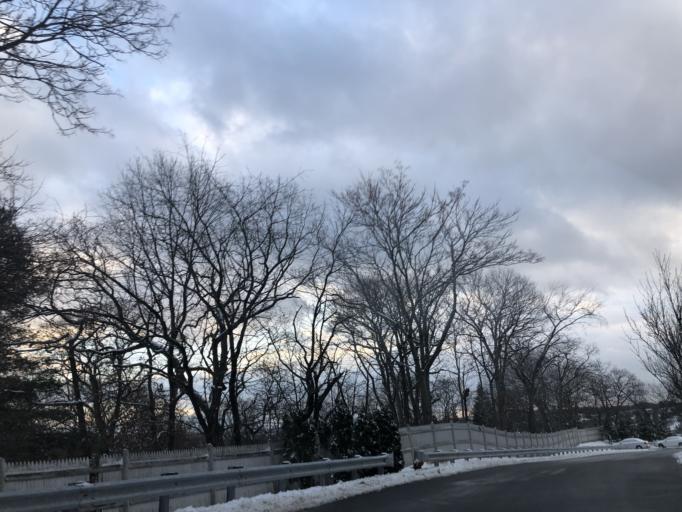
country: US
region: Massachusetts
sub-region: Middlesex County
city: Arlington
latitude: 42.4245
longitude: -71.1605
